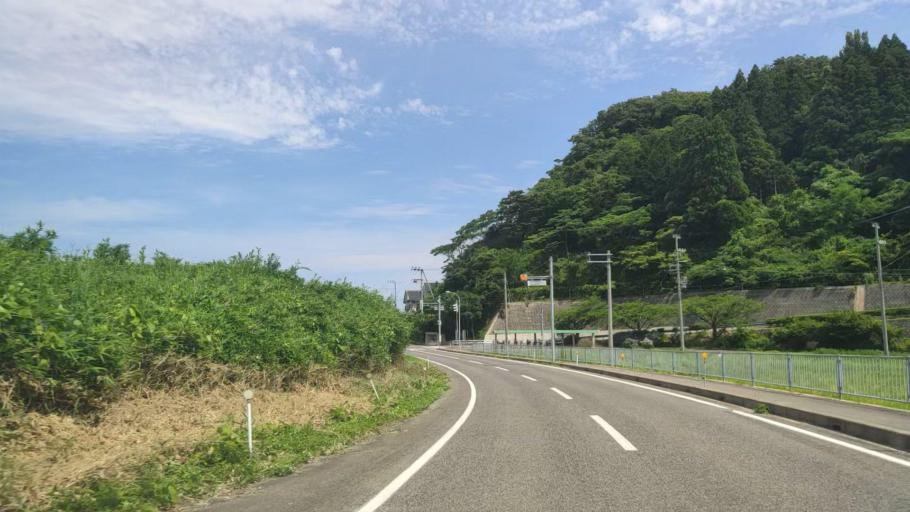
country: JP
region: Hyogo
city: Toyooka
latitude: 35.6514
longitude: 134.7635
